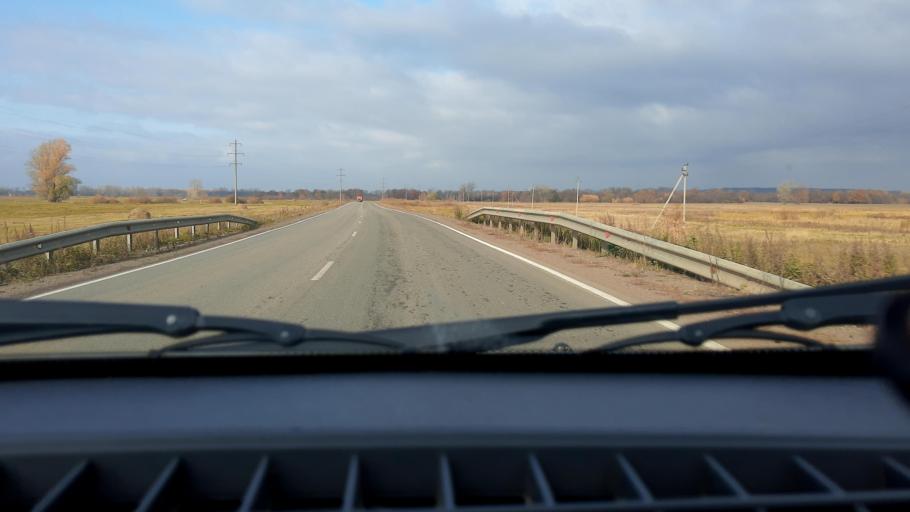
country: RU
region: Bashkortostan
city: Kabakovo
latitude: 54.5593
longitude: 56.0081
